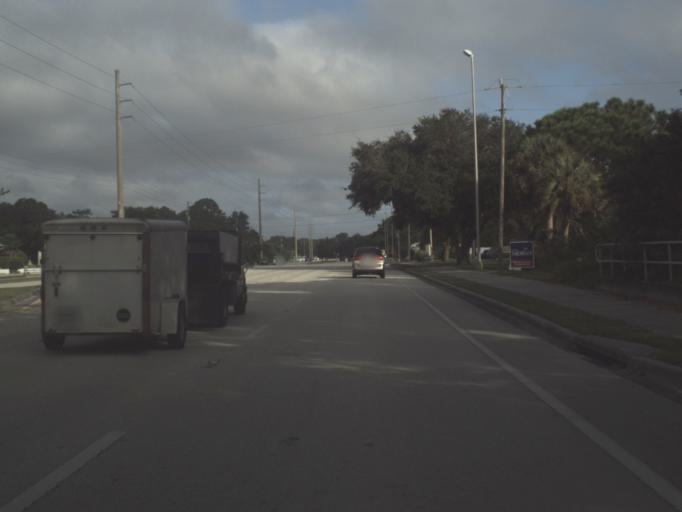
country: US
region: Florida
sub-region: Sarasota County
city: Plantation
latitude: 27.0125
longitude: -82.3838
